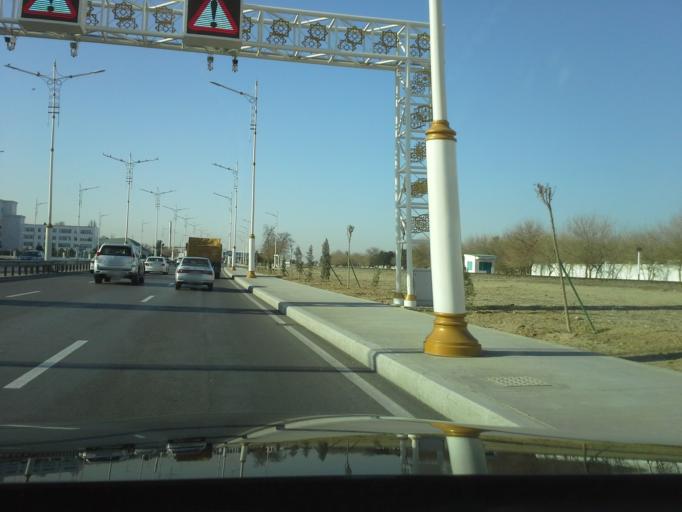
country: TM
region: Ahal
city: Ashgabat
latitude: 37.9562
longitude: 58.3714
